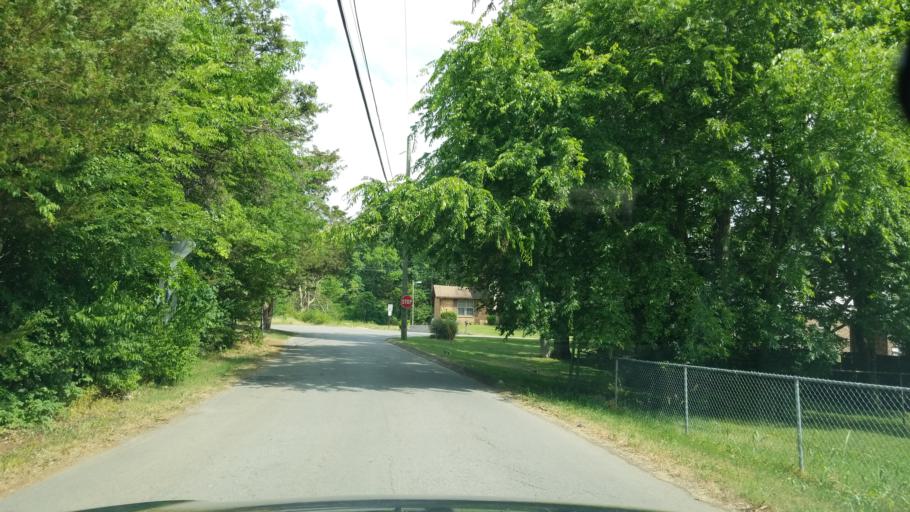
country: US
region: Tennessee
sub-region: Rutherford County
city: La Vergne
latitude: 36.0825
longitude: -86.6180
